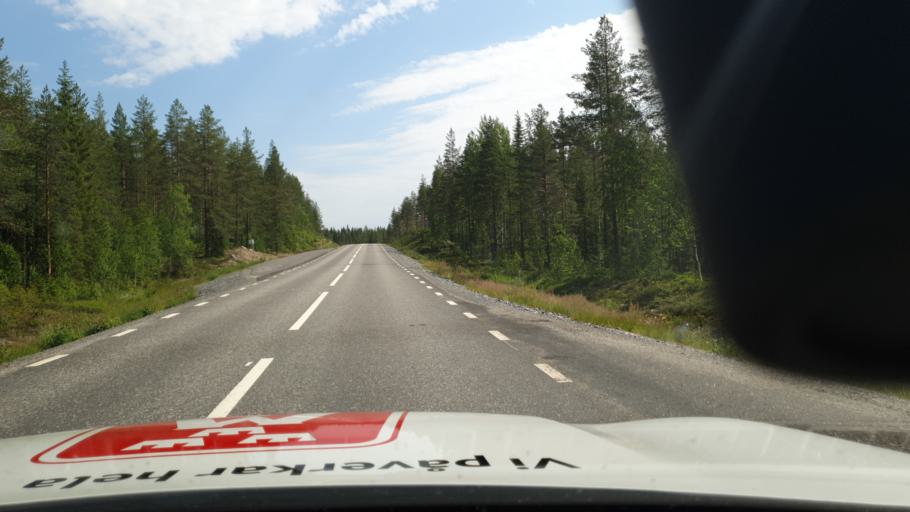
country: SE
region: Vaesterbotten
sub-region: Vindelns Kommun
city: Vindeln
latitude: 64.2496
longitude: 20.0276
